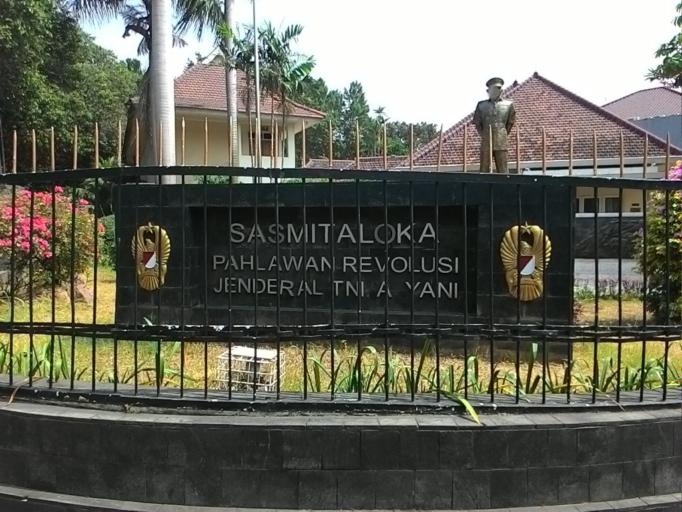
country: ID
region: Jakarta Raya
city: Jakarta
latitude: -6.2048
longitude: 106.8368
